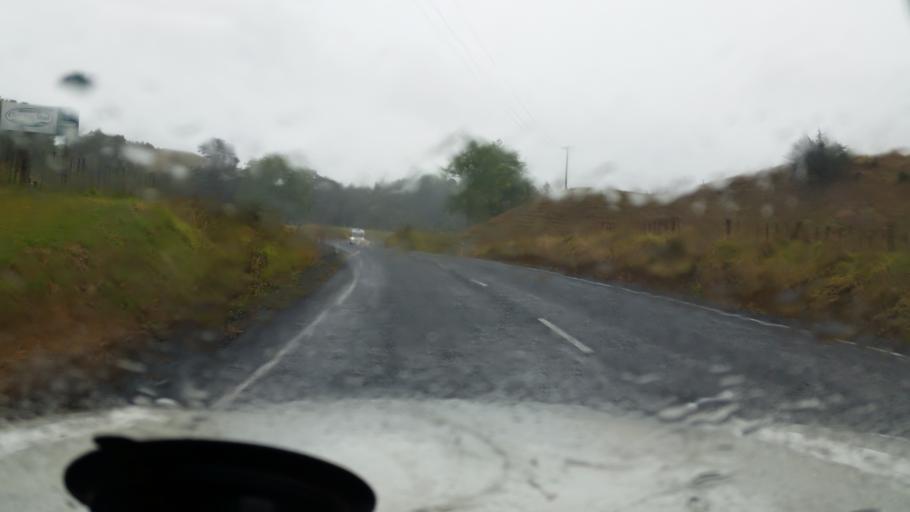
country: NZ
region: Northland
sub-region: Far North District
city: Kaitaia
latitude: -35.2747
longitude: 173.3502
